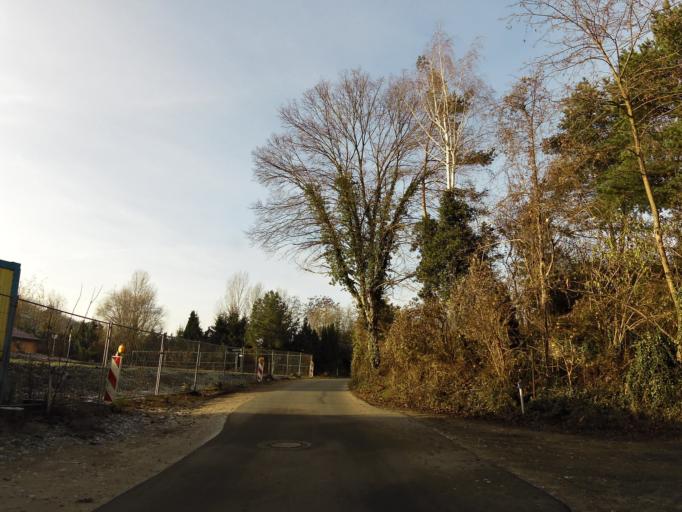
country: DE
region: Brandenburg
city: Werder
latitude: 52.3552
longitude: 12.9212
